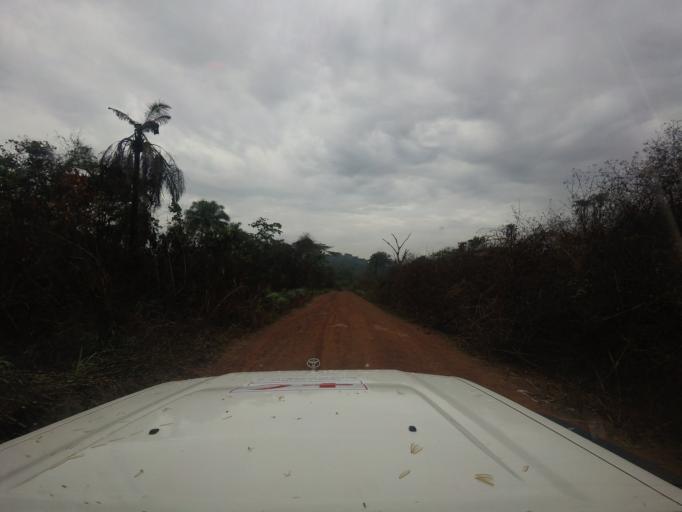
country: LR
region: Lofa
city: Voinjama
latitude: 8.3753
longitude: -9.8673
